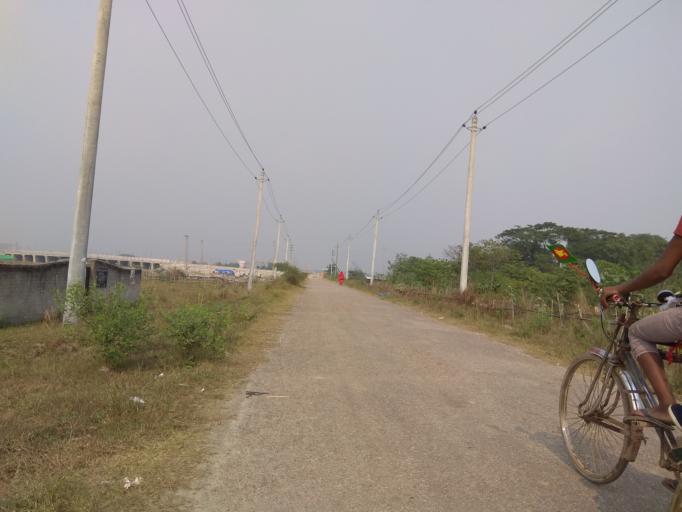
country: BD
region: Dhaka
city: Tungi
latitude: 23.8580
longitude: 90.3725
